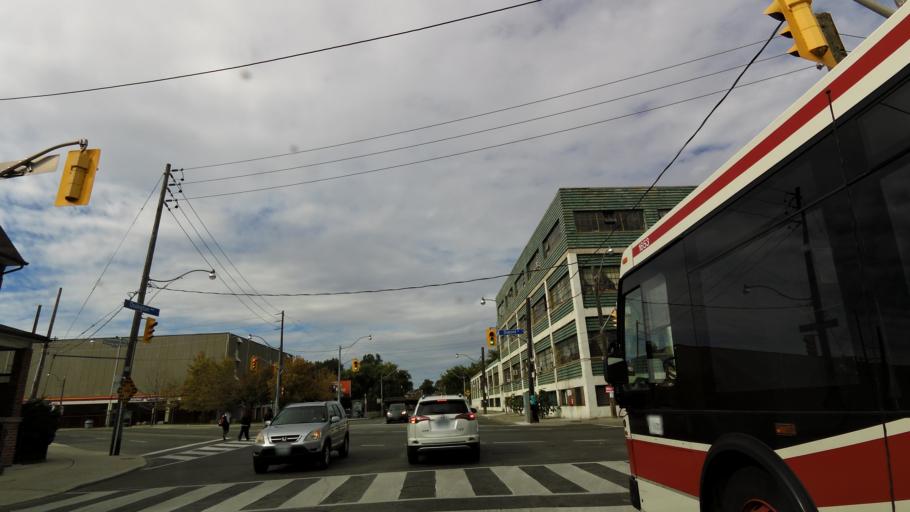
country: CA
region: Ontario
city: Toronto
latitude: 43.6698
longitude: -79.4290
